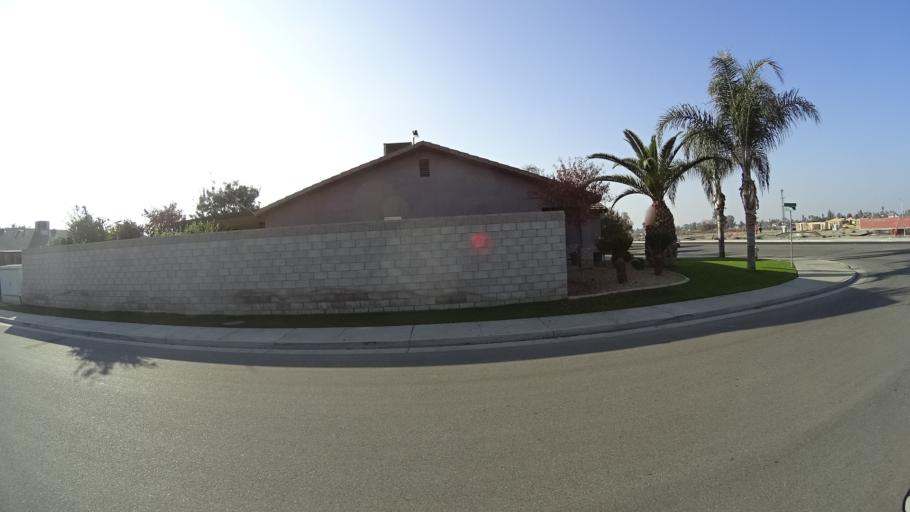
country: US
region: California
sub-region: Kern County
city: Greenfield
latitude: 35.2883
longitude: -119.0163
